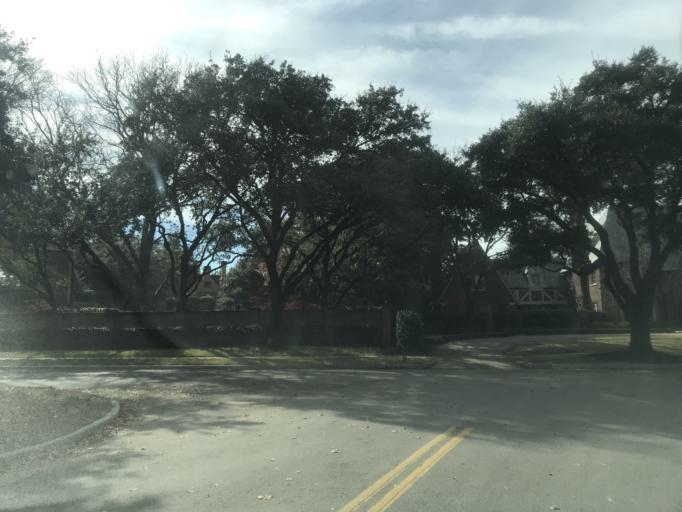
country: US
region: Texas
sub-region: Dallas County
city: Highland Park
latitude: 32.8253
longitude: -96.8035
